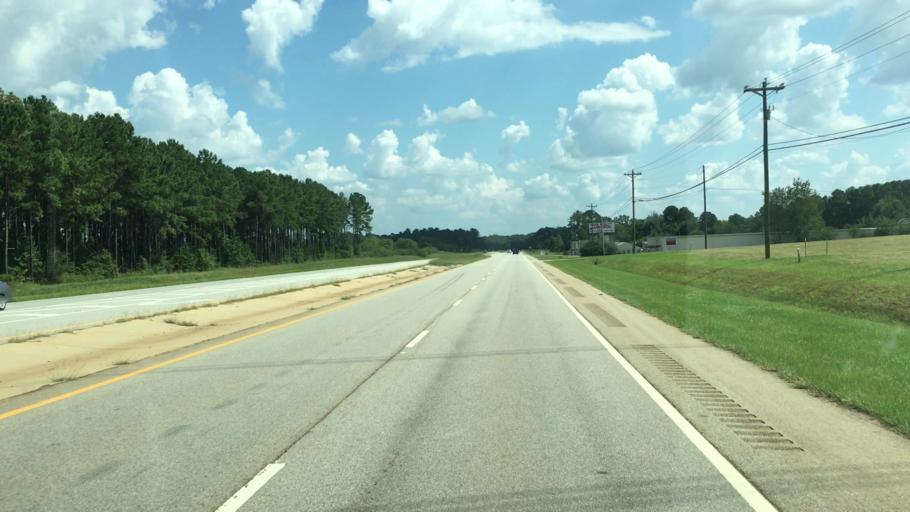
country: US
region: Georgia
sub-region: Putnam County
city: Eatonton
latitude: 33.2532
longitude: -83.3286
